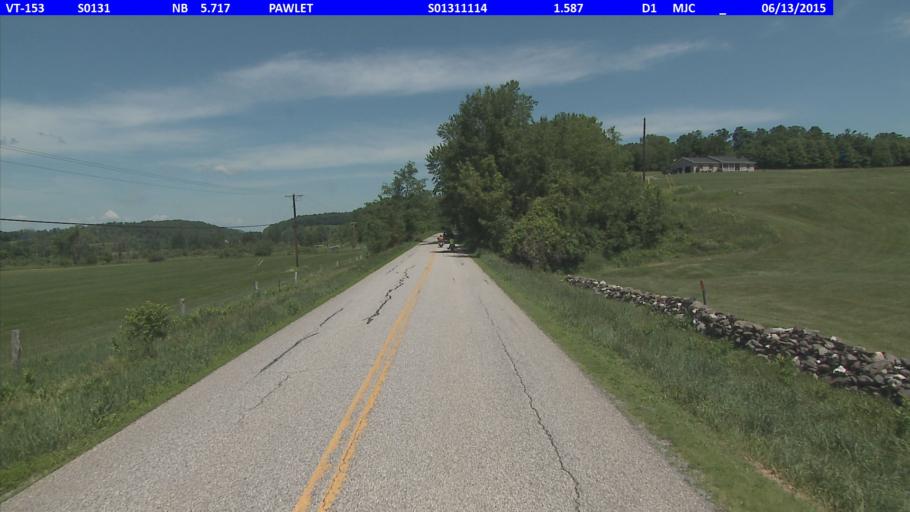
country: US
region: New York
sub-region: Washington County
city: Granville
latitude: 43.3368
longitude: -73.2434
